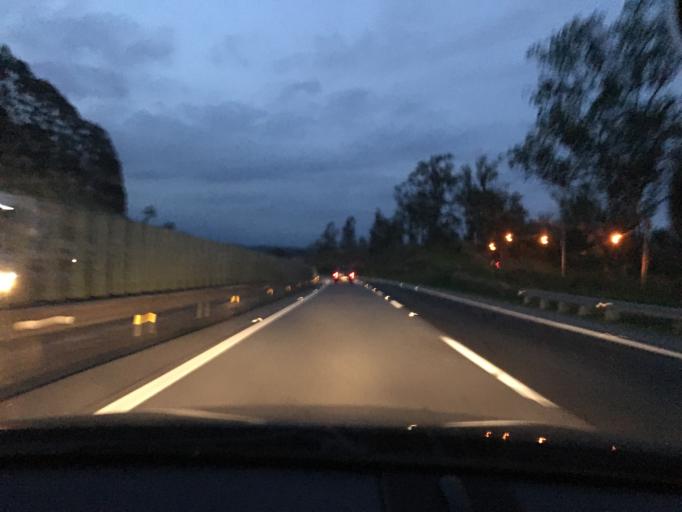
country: BR
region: Sao Paulo
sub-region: Santa Isabel
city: Santa Isabel
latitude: -23.3554
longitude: -46.1255
